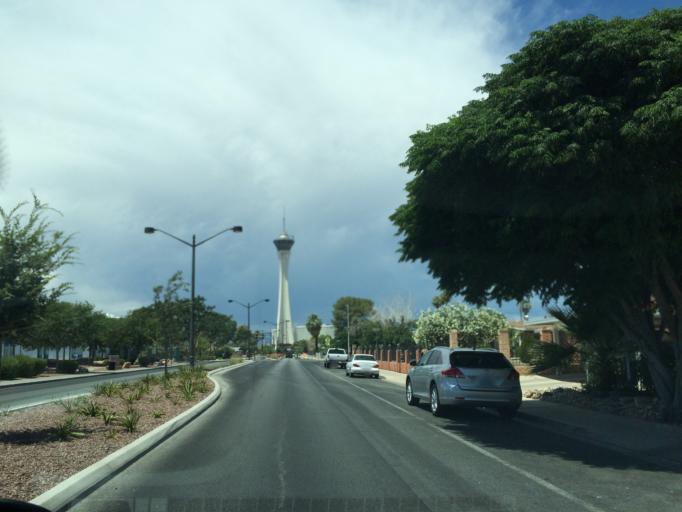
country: US
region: Nevada
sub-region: Clark County
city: Las Vegas
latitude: 36.1480
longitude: -115.1404
